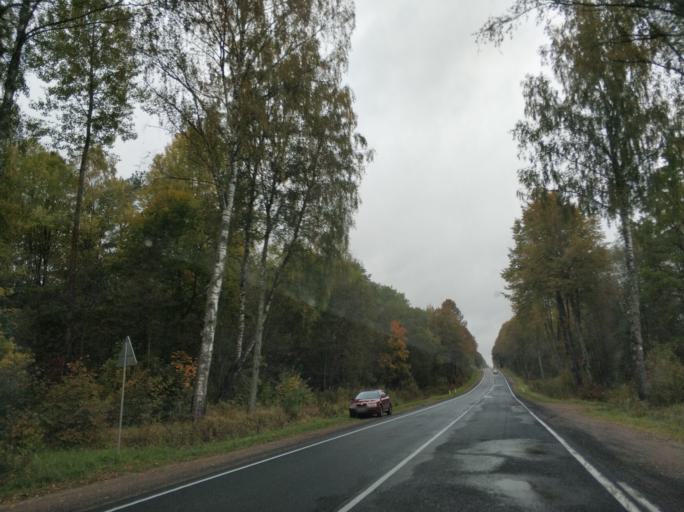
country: RU
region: Pskov
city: Opochka
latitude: 56.5561
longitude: 28.6318
